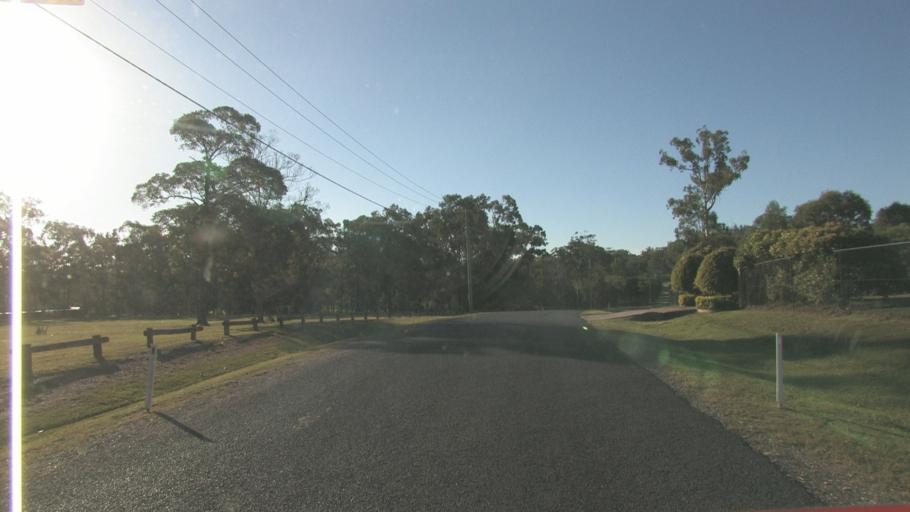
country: AU
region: Queensland
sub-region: Redland
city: Redland Bay
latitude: -27.6620
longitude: 153.2675
